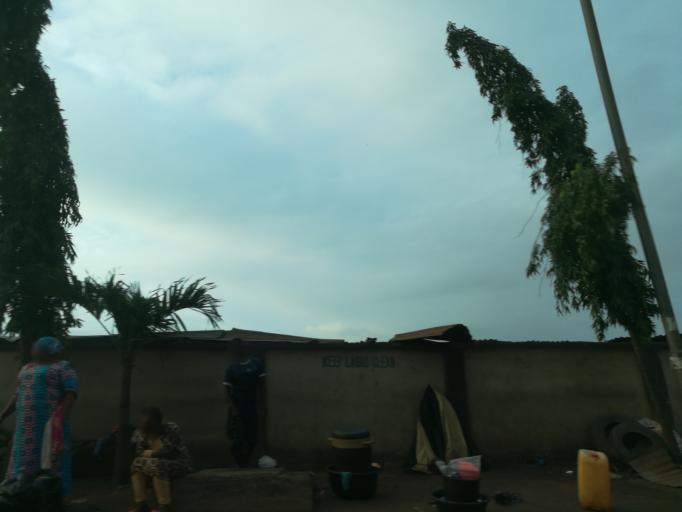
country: NG
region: Lagos
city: Ojota
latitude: 6.5958
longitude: 3.3831
